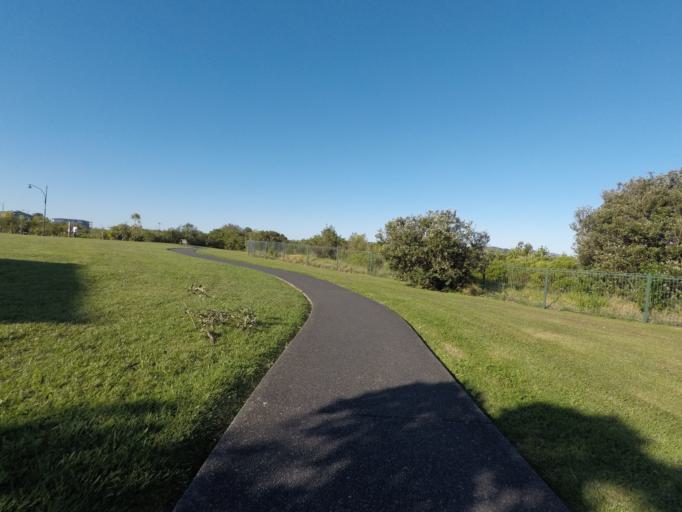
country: NZ
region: Auckland
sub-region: Auckland
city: Rosebank
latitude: -36.8388
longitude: 174.6613
